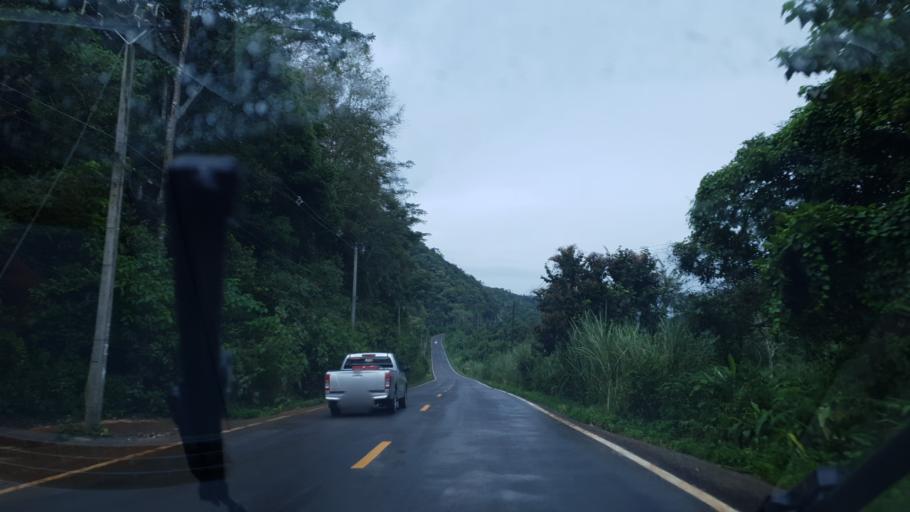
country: TH
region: Mae Hong Son
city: Ban Huai I Huak
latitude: 18.1476
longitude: 98.0993
